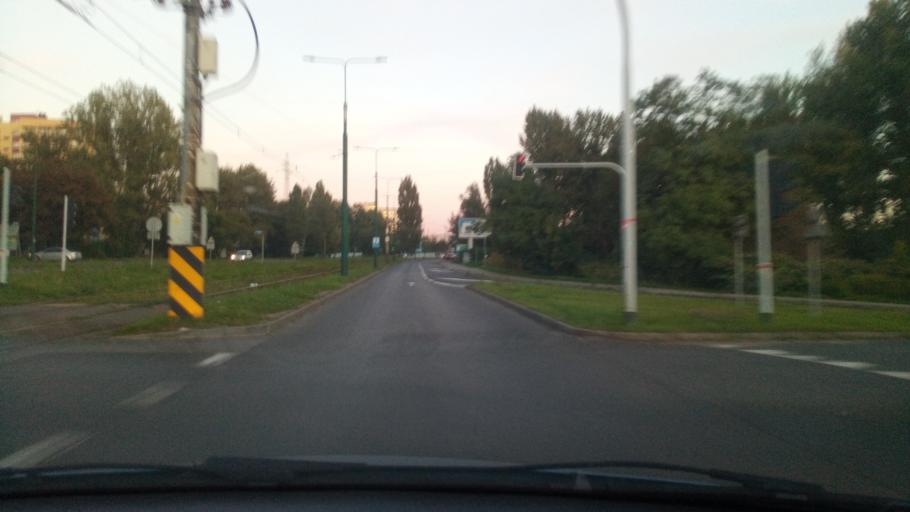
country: PL
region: Silesian Voivodeship
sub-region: Sosnowiec
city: Sosnowiec
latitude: 50.2880
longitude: 19.1004
